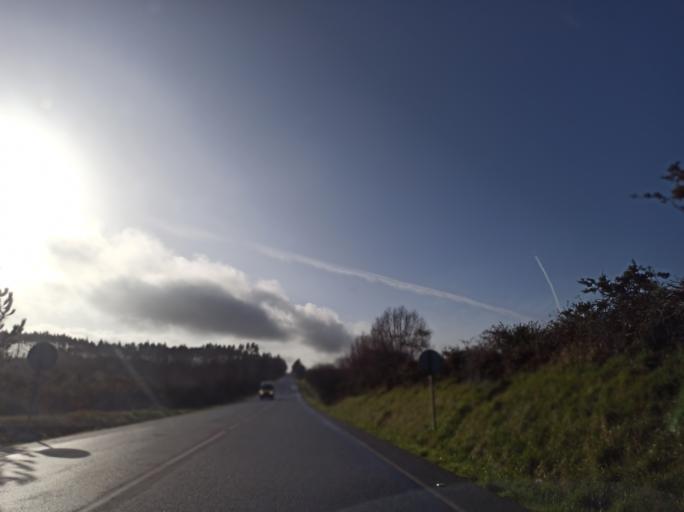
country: ES
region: Galicia
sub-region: Provincia da Coruna
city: Curtis
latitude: 43.1133
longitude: -8.0262
